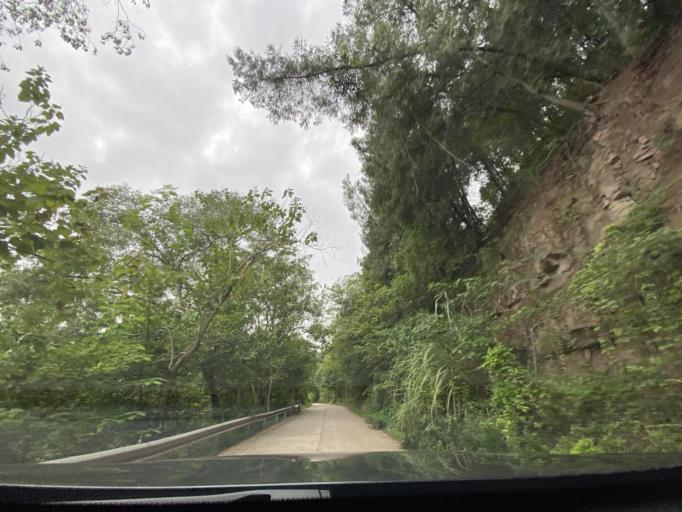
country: CN
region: Sichuan
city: Jiancheng
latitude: 30.3884
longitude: 104.5130
